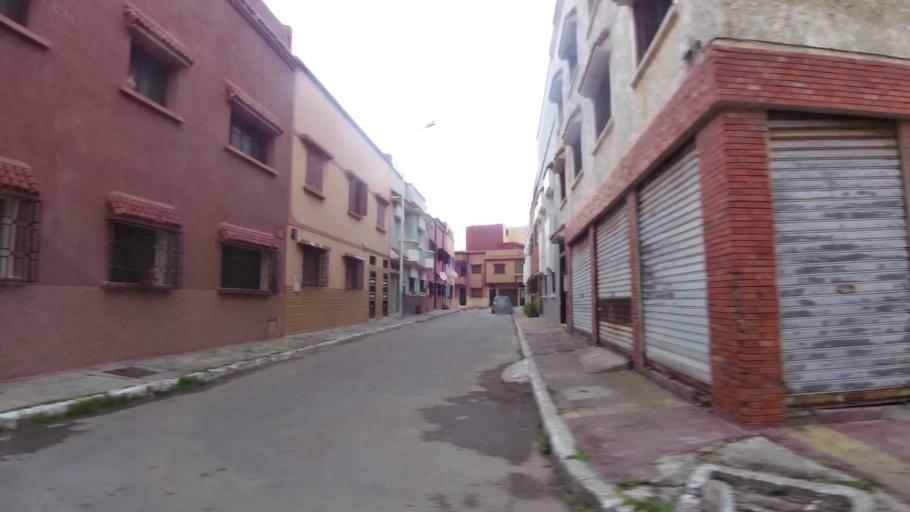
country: MA
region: Doukkala-Abda
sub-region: El-Jadida
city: El Jadida
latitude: 33.2484
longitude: -8.5269
